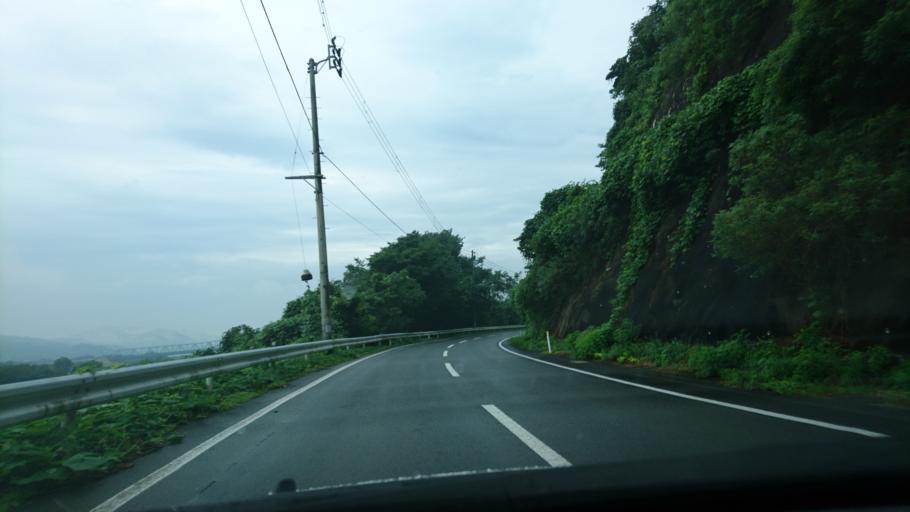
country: JP
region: Iwate
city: Ichinoseki
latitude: 38.8915
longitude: 141.2658
